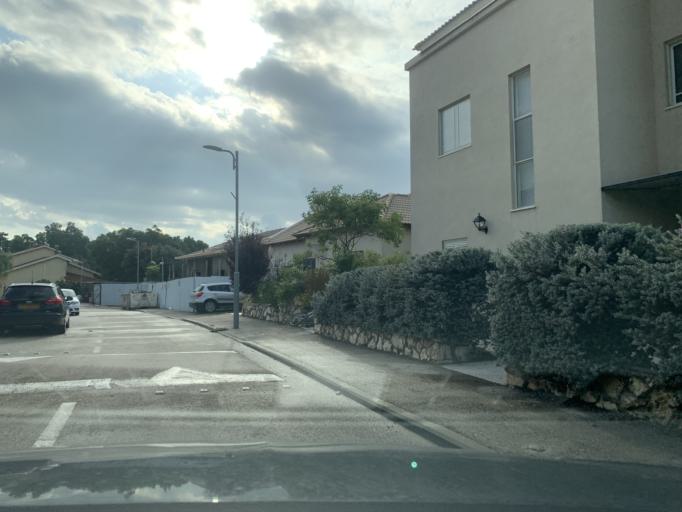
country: IL
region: Central District
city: Rosh Ha'Ayin
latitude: 32.0636
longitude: 34.9503
